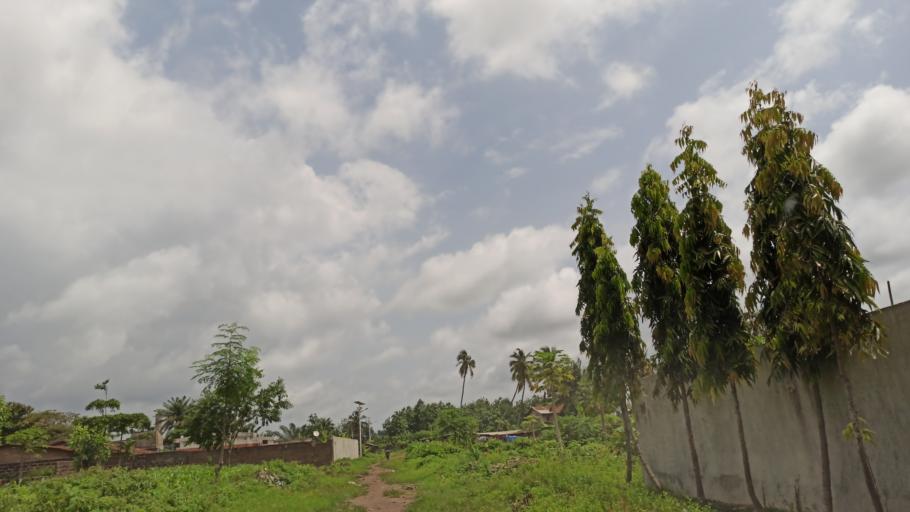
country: BJ
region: Queme
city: Porto-Novo
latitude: 6.4674
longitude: 2.6305
